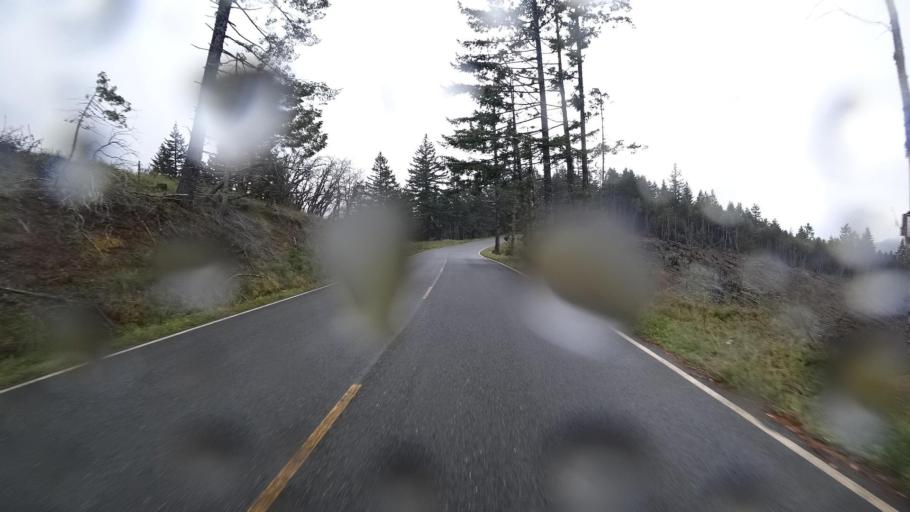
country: US
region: California
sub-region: Humboldt County
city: Westhaven-Moonstone
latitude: 41.1465
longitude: -123.8351
